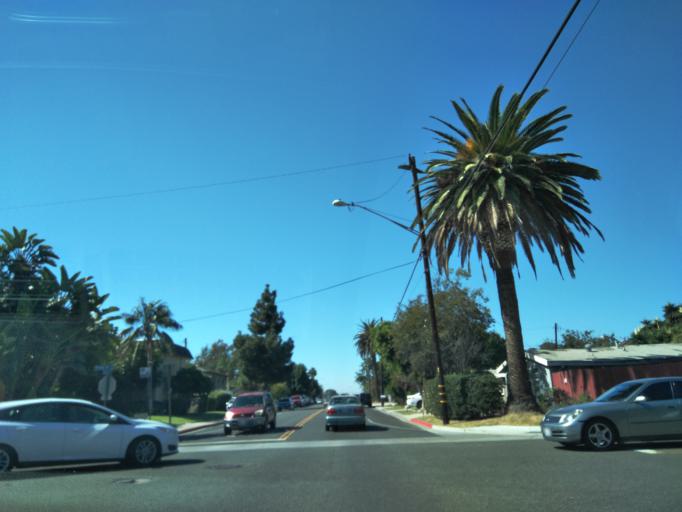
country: US
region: California
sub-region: Orange County
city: Costa Mesa
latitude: 33.6606
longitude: -117.8937
